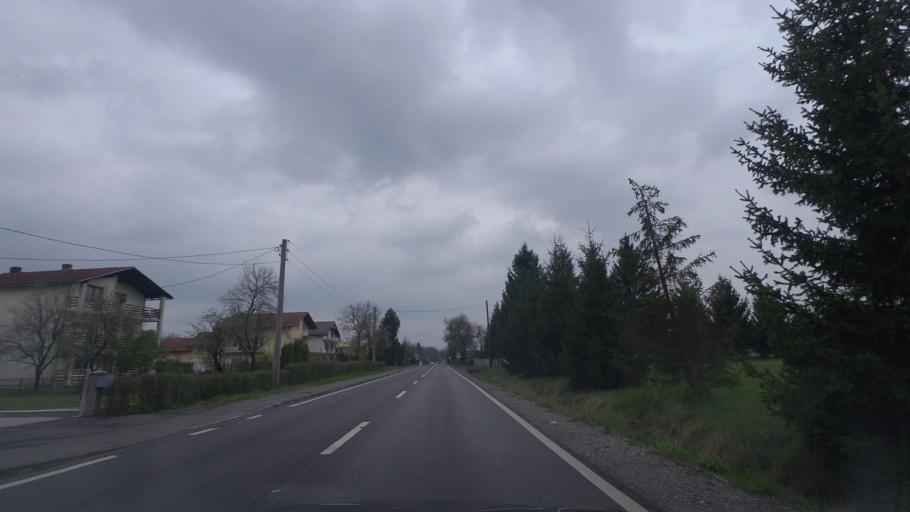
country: HR
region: Karlovacka
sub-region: Grad Karlovac
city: Karlovac
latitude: 45.5562
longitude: 15.5766
